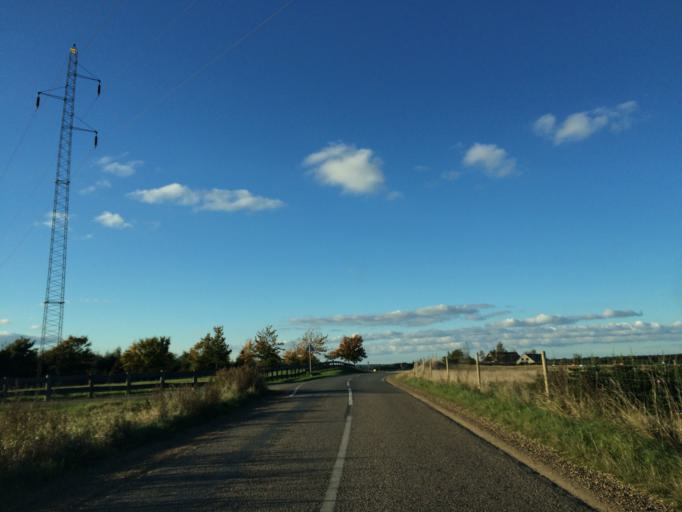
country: DK
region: Central Jutland
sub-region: Silkeborg Kommune
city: Svejbaek
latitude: 56.1435
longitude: 9.7076
